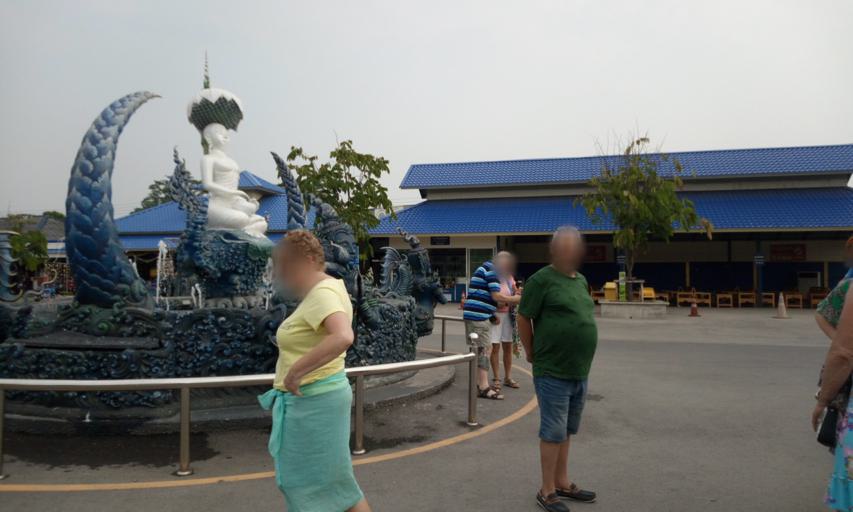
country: TH
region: Chiang Rai
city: Chiang Rai
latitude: 19.9234
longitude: 99.8422
